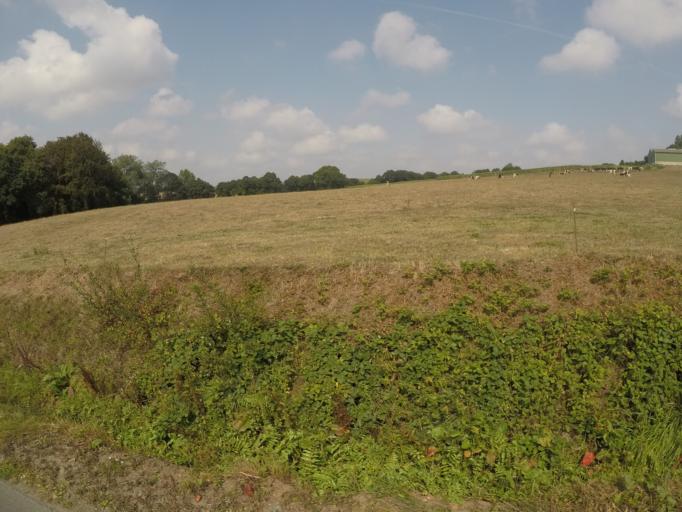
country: FR
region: Brittany
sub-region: Departement des Cotes-d'Armor
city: Saint-Donan
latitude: 48.5146
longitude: -2.9073
